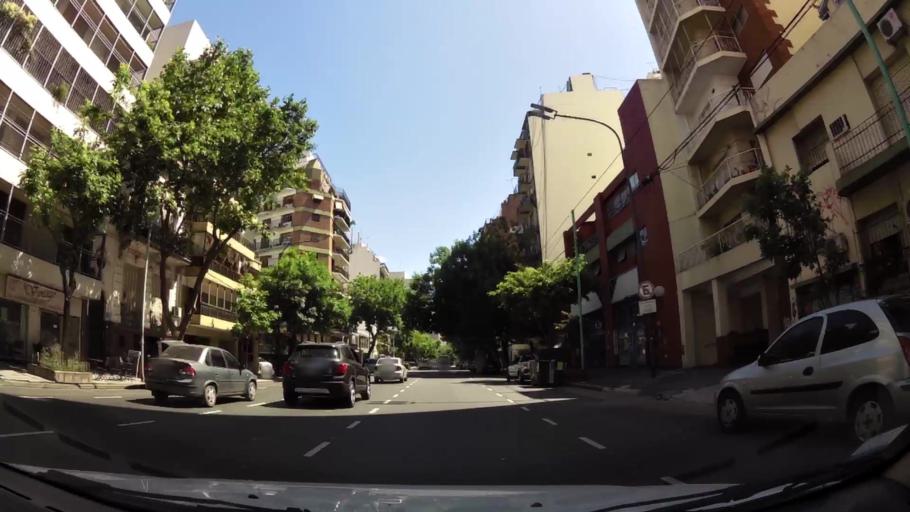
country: AR
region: Buenos Aires F.D.
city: Villa Santa Rita
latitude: -34.6240
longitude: -58.4454
